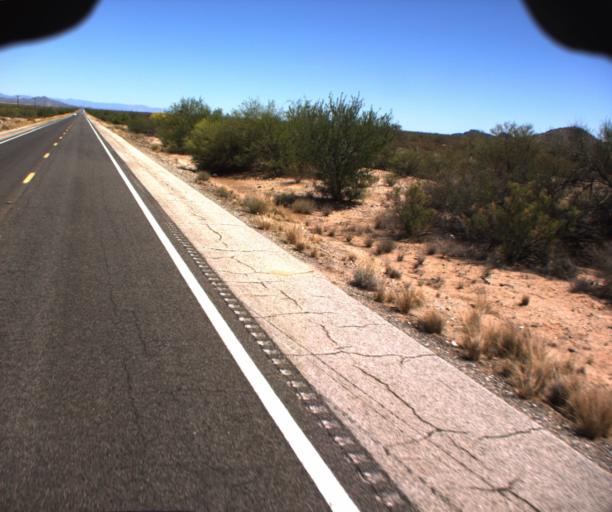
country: US
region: Arizona
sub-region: La Paz County
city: Salome
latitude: 33.9111
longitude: -113.2749
